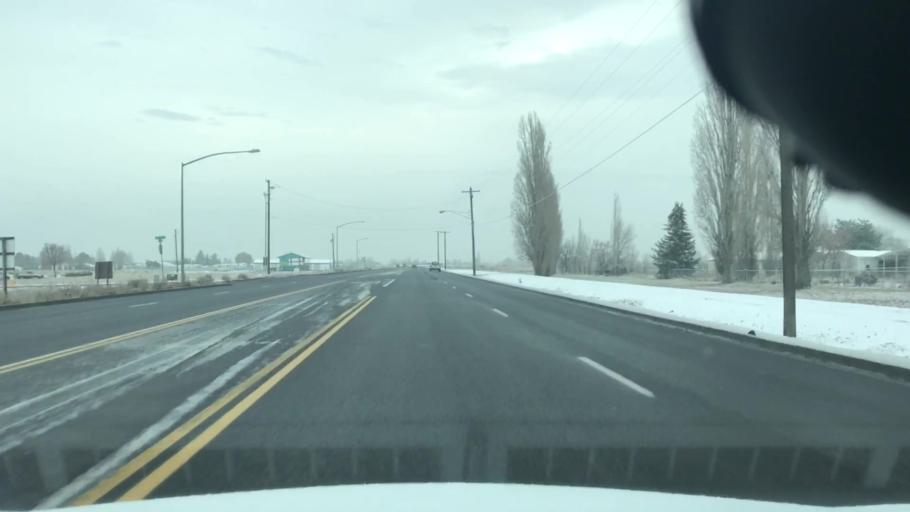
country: US
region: Washington
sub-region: Grant County
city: Cascade Valley
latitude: 47.1624
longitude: -119.3133
